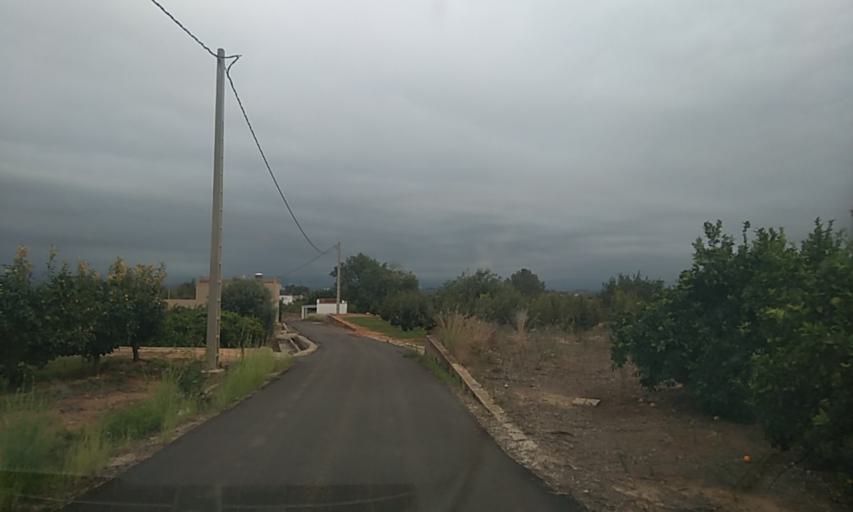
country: ES
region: Valencia
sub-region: Provincia de Valencia
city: Benimodo
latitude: 39.1937
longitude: -0.5629
